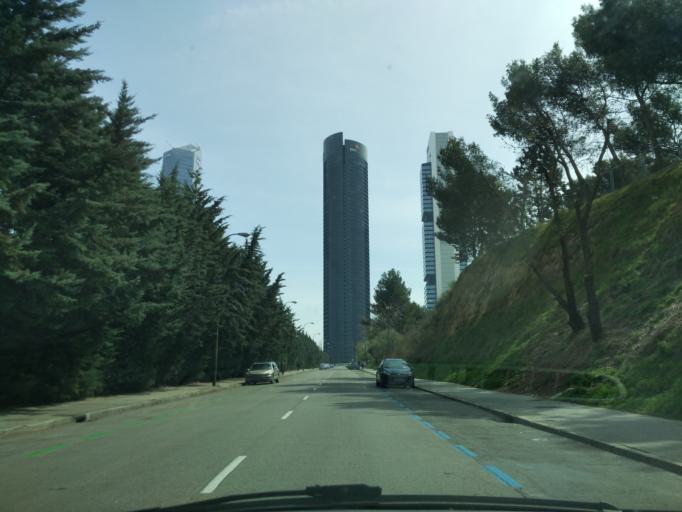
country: ES
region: Madrid
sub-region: Provincia de Madrid
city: Tetuan de las Victorias
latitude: 40.4776
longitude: -3.6952
